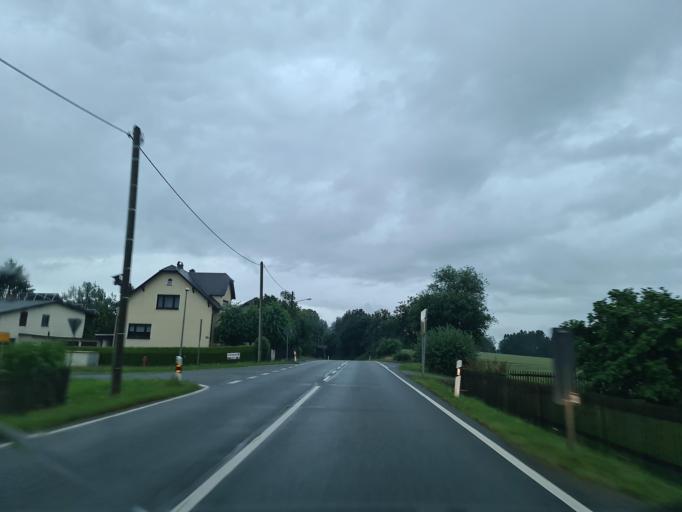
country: DE
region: Saxony
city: Limbach
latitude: 50.5403
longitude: 12.2551
